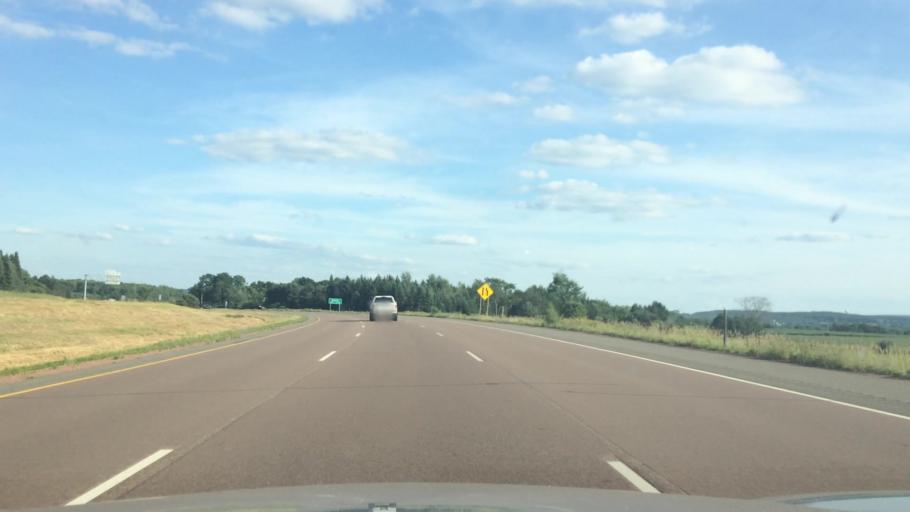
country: US
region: Wisconsin
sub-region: Marathon County
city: Wausau
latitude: 45.0152
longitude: -89.6682
